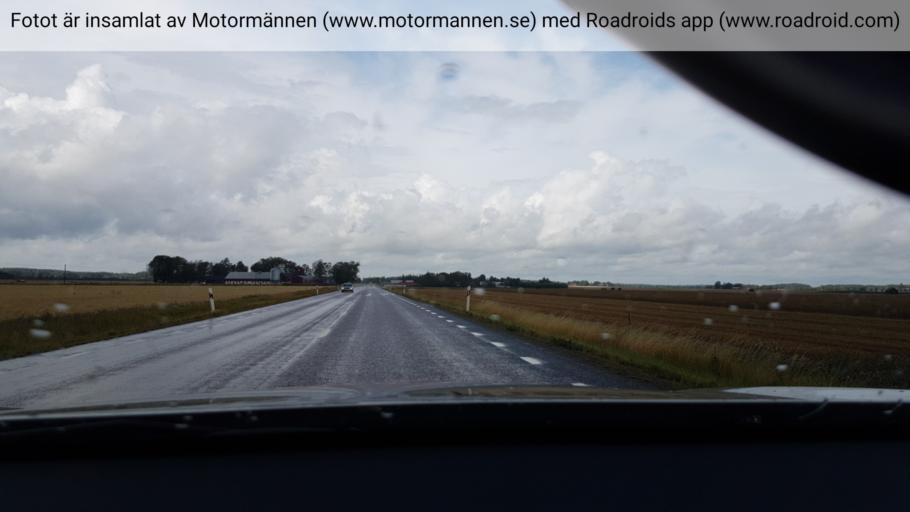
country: SE
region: Uppsala
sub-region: Uppsala Kommun
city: Gamla Uppsala
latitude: 59.9130
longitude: 17.5285
